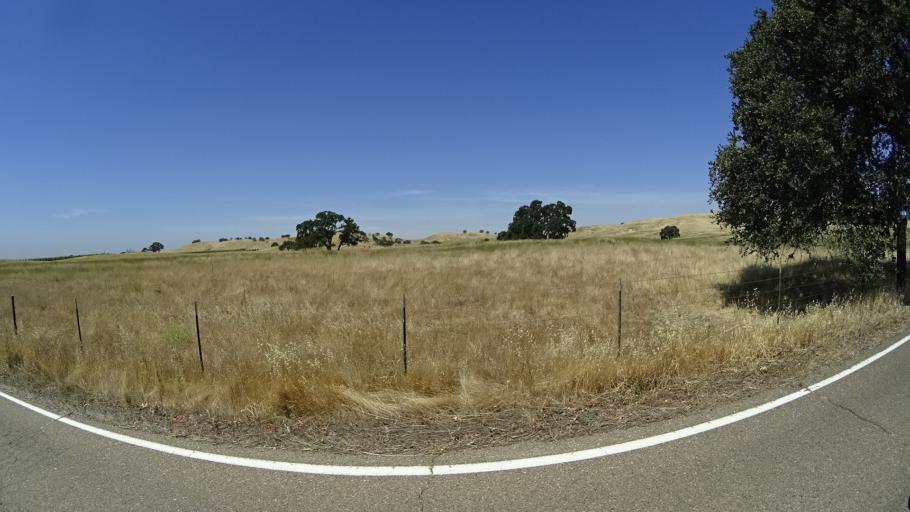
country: US
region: California
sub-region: Calaveras County
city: Rancho Calaveras
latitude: 38.1152
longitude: -120.9447
